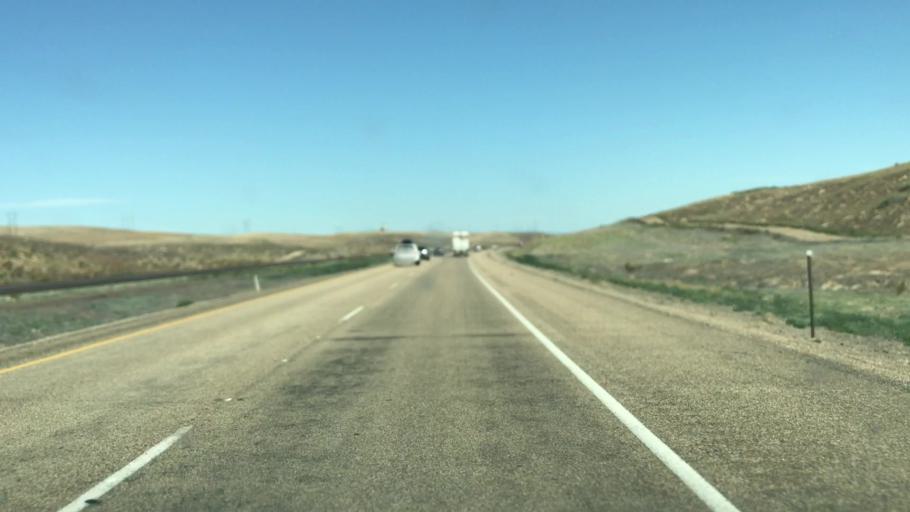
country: US
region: Idaho
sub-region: Payette County
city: New Plymouth
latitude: 43.8824
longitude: -116.7993
